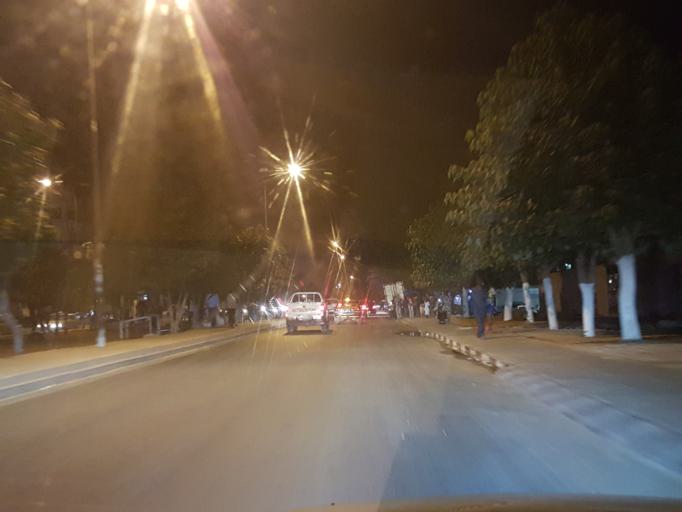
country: SN
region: Dakar
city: Grand Dakar
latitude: 14.7325
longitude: -17.4600
